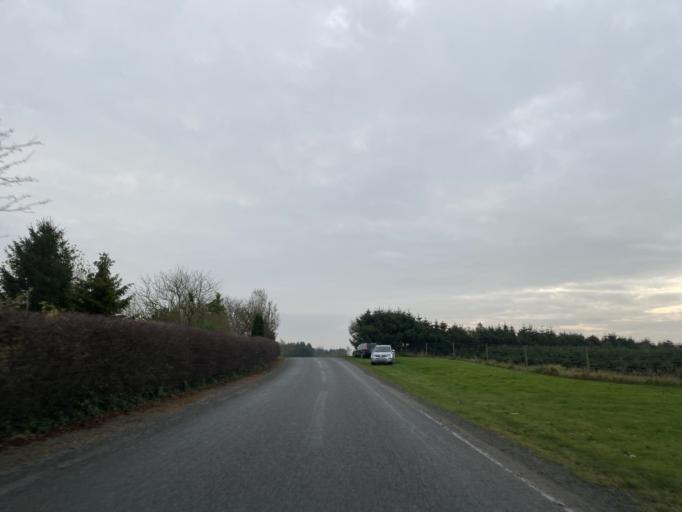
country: DK
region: Central Jutland
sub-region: Skanderborg Kommune
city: Ry
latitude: 56.1425
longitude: 9.7089
